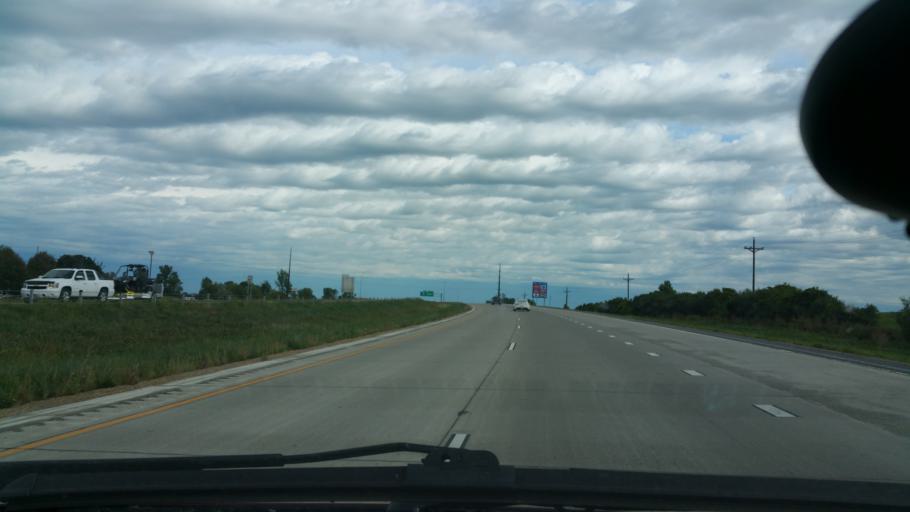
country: US
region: Minnesota
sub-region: Steele County
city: Owatonna
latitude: 44.0883
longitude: -93.2448
